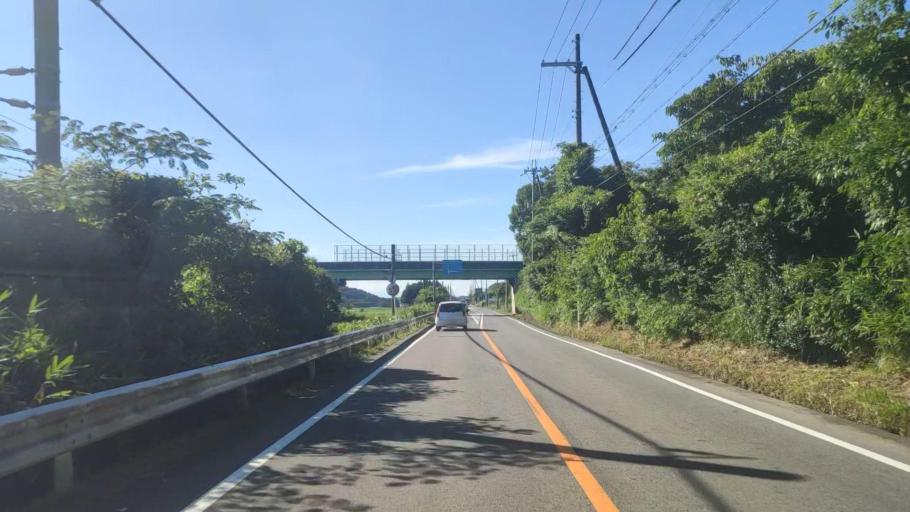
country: JP
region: Shiga Prefecture
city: Minakuchicho-matoba
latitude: 34.8755
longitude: 136.2398
